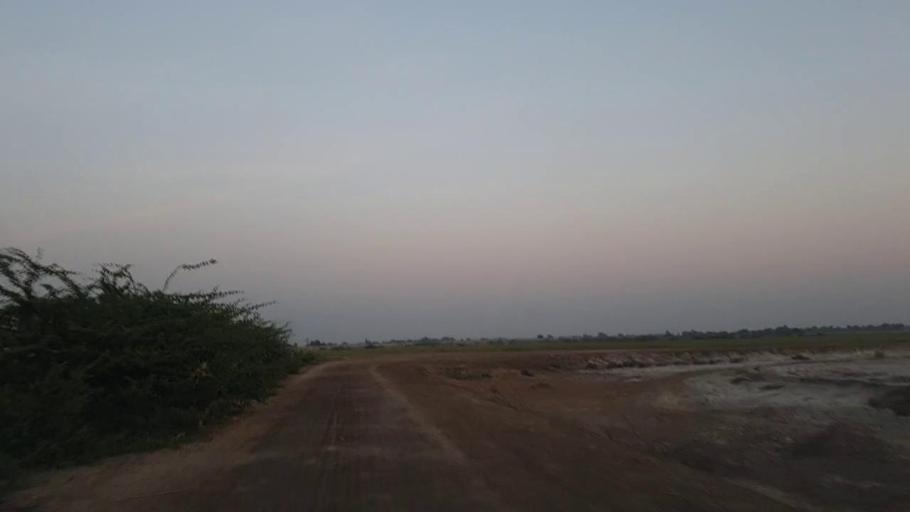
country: PK
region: Sindh
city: Naukot
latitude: 24.9966
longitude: 69.4327
